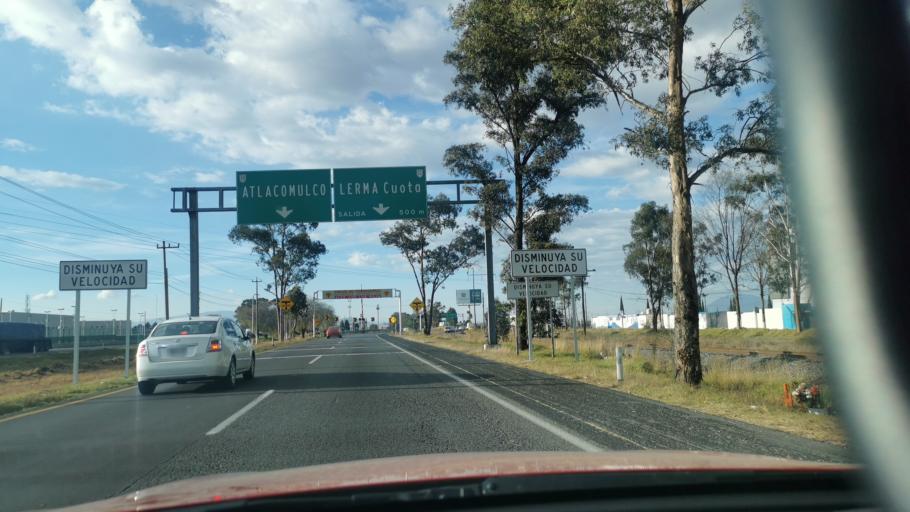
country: MX
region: Mexico
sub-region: Toluca
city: Colonia Aviacion Autopan
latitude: 19.3797
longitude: -99.7032
